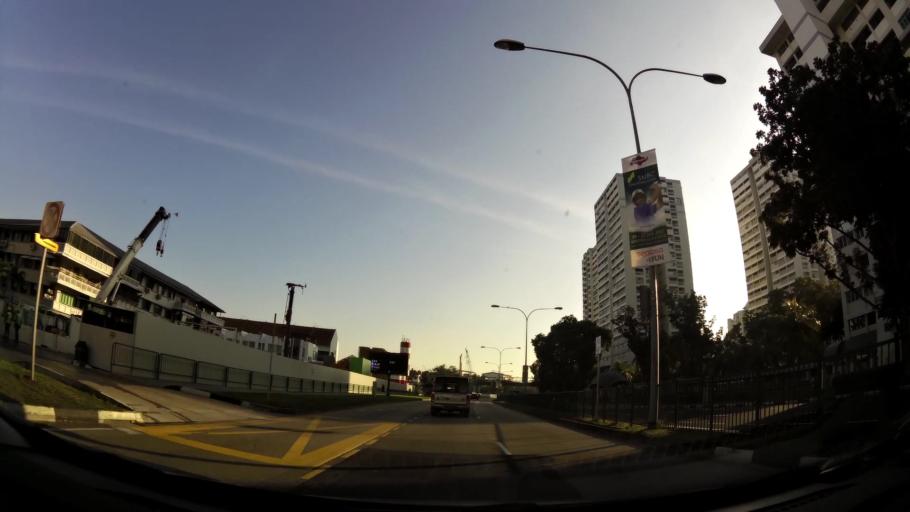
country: SG
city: Singapore
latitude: 1.3042
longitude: 103.9073
